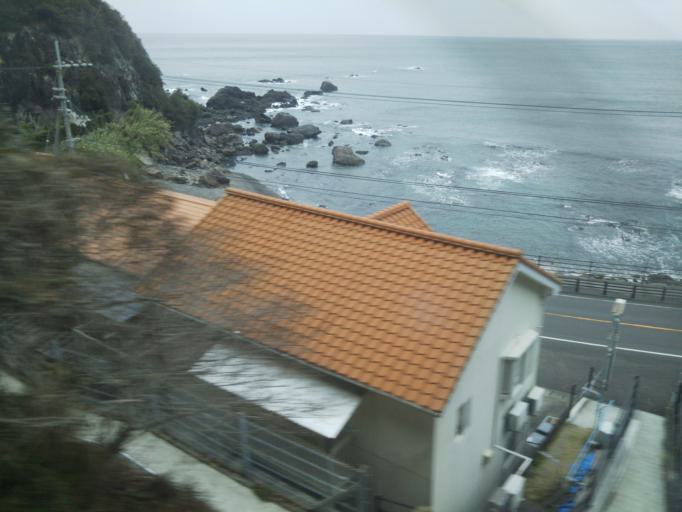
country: JP
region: Kochi
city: Nakamura
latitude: 33.0542
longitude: 133.0972
